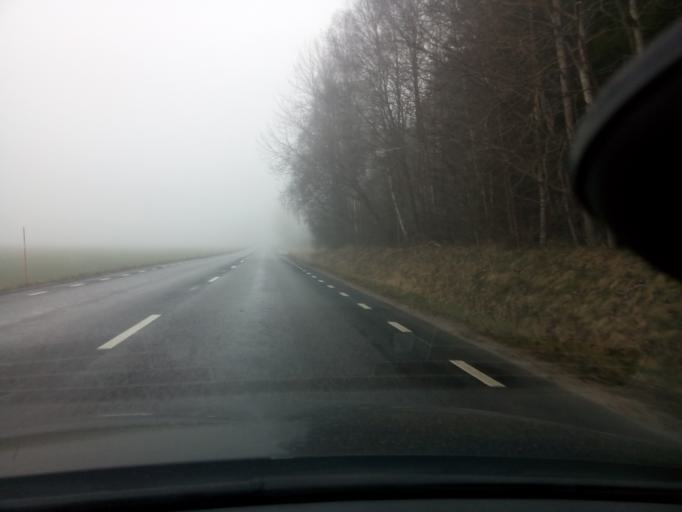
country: SE
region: Soedermanland
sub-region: Nykopings Kommun
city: Nykoping
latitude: 58.8077
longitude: 17.0814
